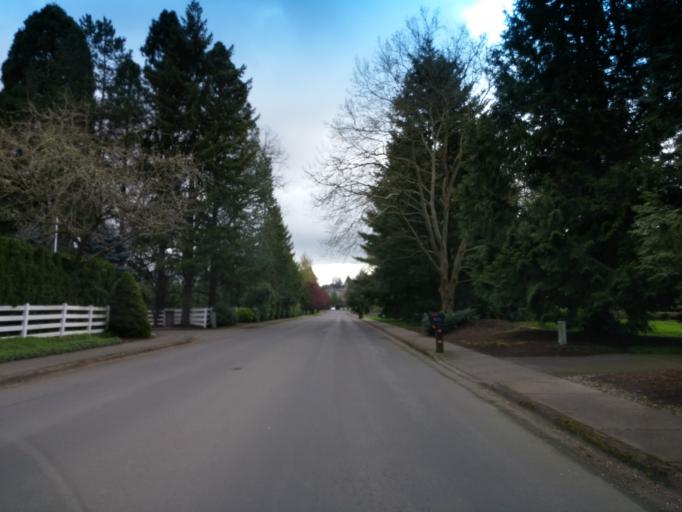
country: US
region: Oregon
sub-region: Washington County
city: Cedar Mill
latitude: 45.5368
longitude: -122.8181
